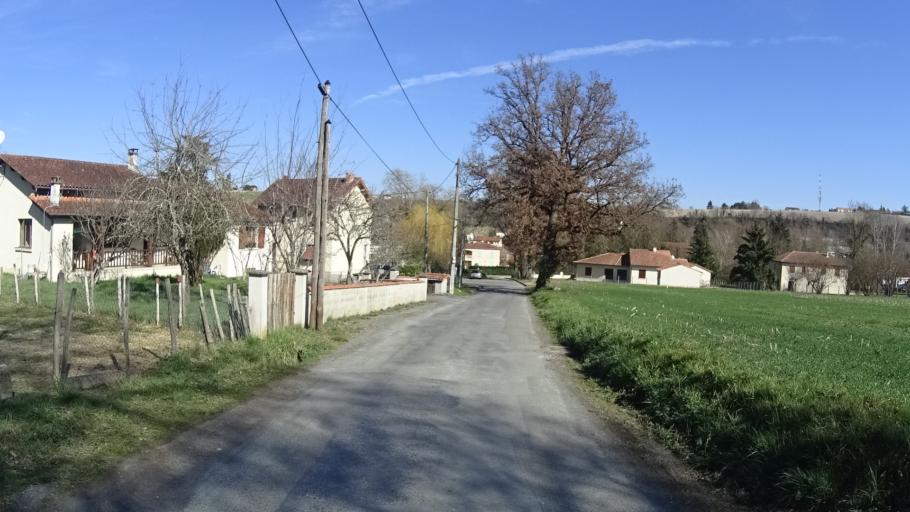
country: FR
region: Aquitaine
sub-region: Departement de la Dordogne
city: Riberac
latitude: 45.2413
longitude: 0.3408
